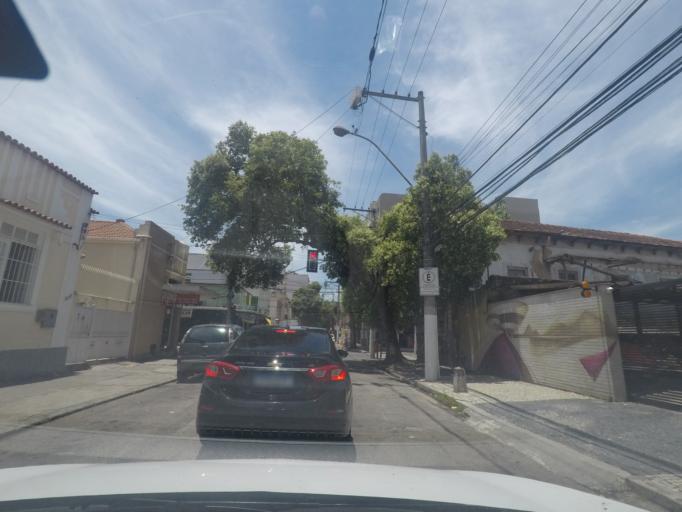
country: BR
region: Rio de Janeiro
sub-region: Niteroi
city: Niteroi
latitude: -22.8869
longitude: -43.1229
